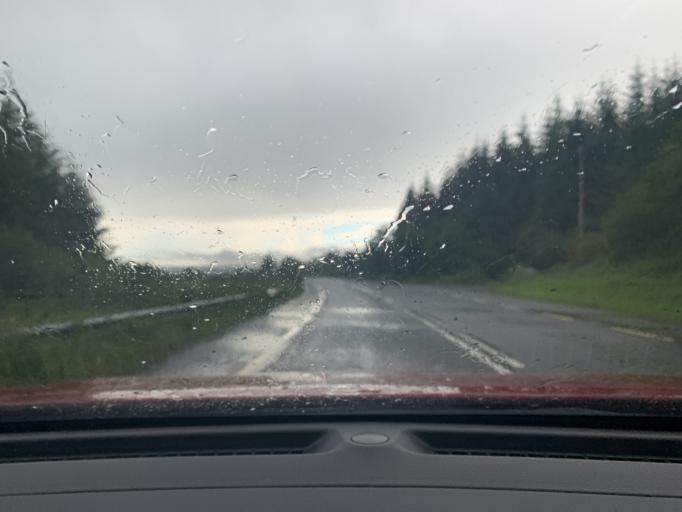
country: IE
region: Ulster
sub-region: County Donegal
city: Letterkenny
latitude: 54.8834
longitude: -7.7383
